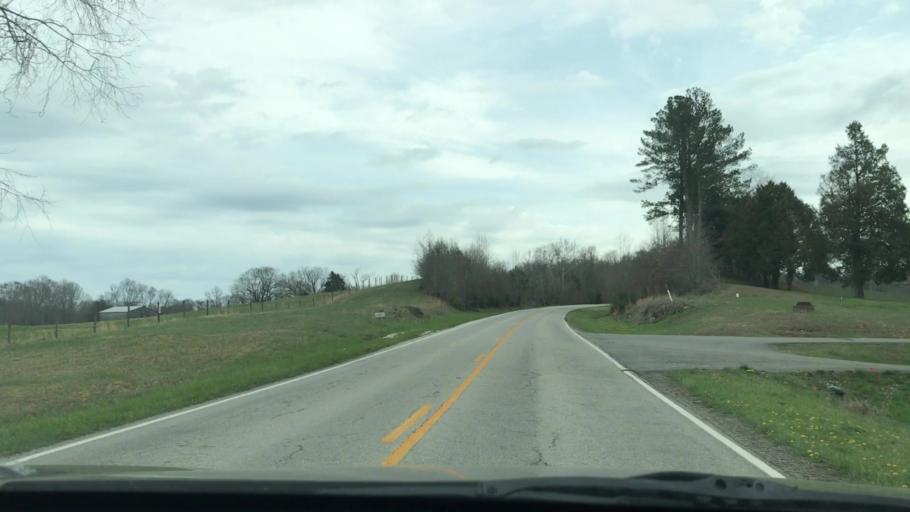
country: US
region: Kentucky
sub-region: Hart County
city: Munfordville
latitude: 37.3157
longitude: -85.7625
